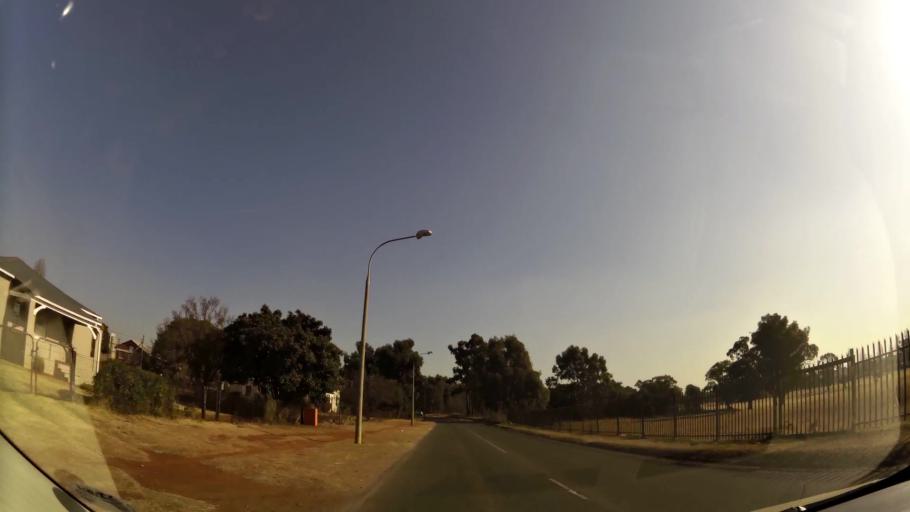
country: ZA
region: Gauteng
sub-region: West Rand District Municipality
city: Randfontein
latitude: -26.1583
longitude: 27.7136
